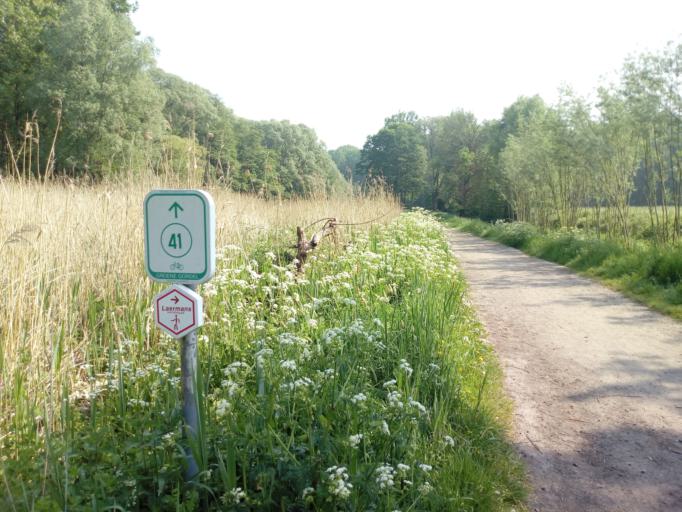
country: BE
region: Flanders
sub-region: Provincie Vlaams-Brabant
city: Bever
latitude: 50.9113
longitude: 4.3164
